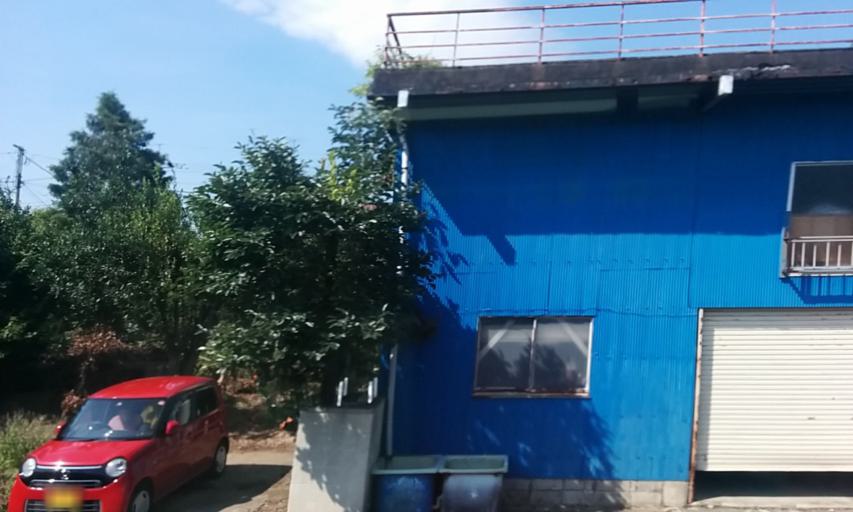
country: JP
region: Saitama
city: Kazo
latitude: 36.1344
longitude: 139.5788
